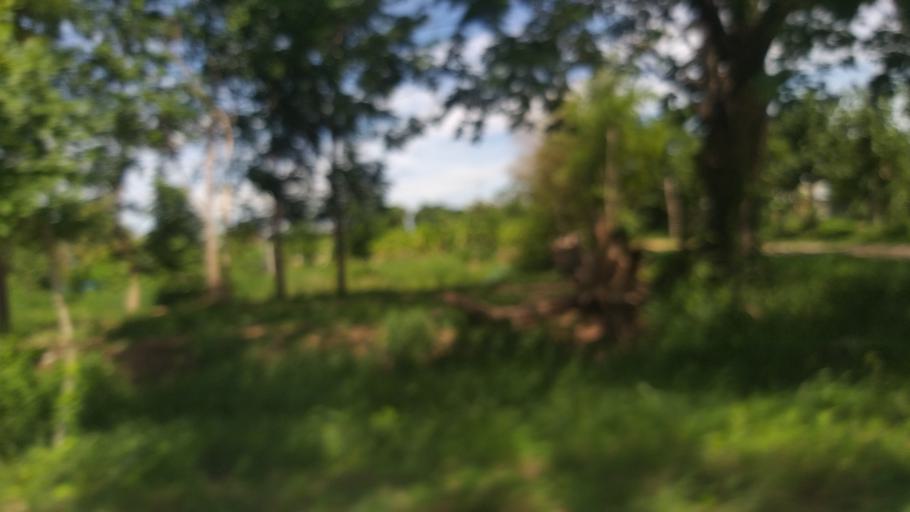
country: TH
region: Khon Kaen
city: Nong Ruea
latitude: 16.4597
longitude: 102.4413
